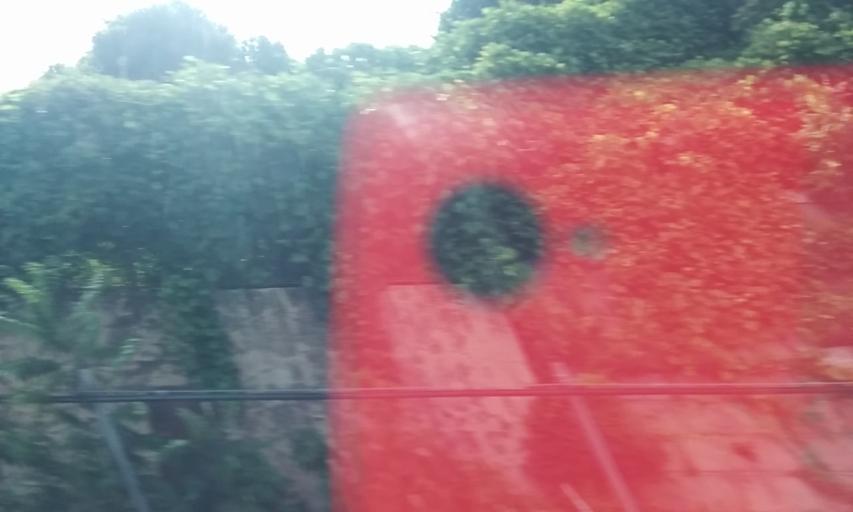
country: JP
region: Fukushima
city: Motomiya
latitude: 37.5030
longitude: 140.4266
